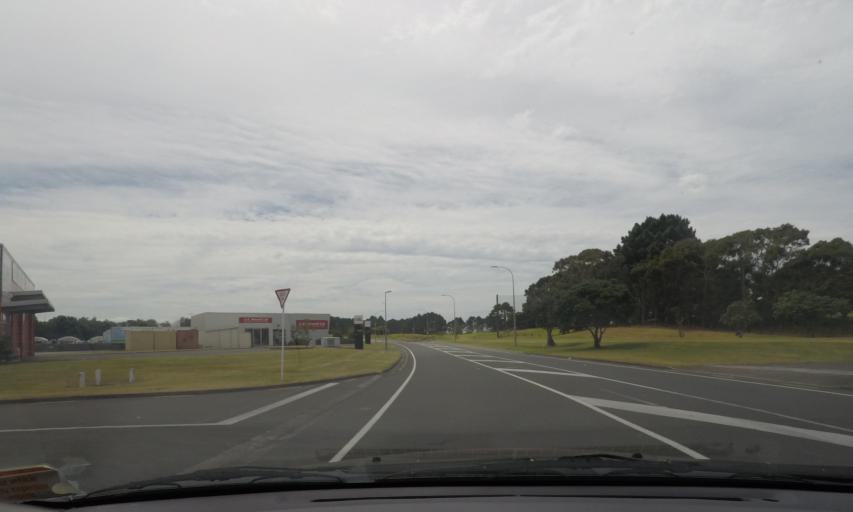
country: NZ
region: Auckland
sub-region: Auckland
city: Mangere
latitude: -36.9983
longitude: 174.8002
